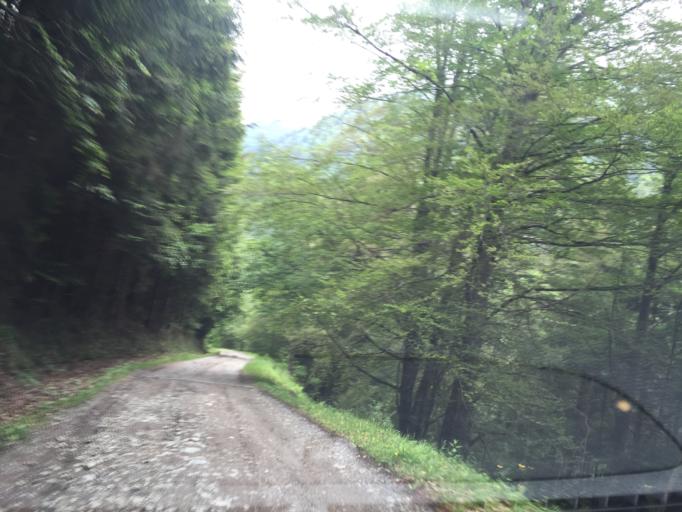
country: FR
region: Rhone-Alpes
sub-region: Departement de la Savoie
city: La Rochette
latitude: 45.4363
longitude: 6.1720
